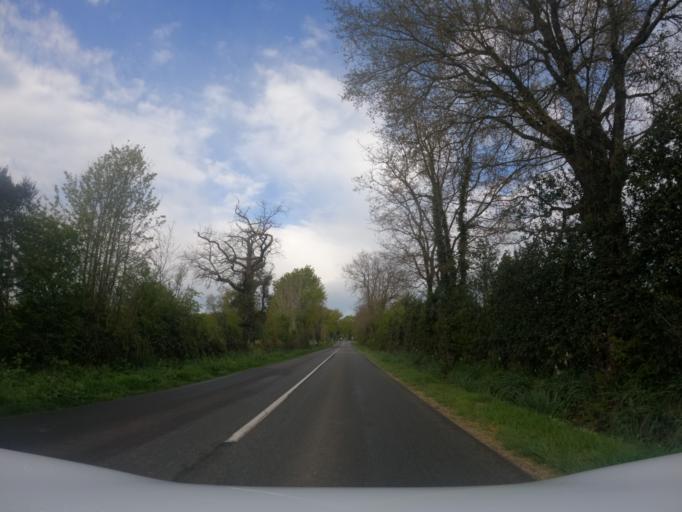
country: FR
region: Pays de la Loire
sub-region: Departement de la Vendee
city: Saint-Vincent-sur-Graon
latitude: 46.5413
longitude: -1.3813
